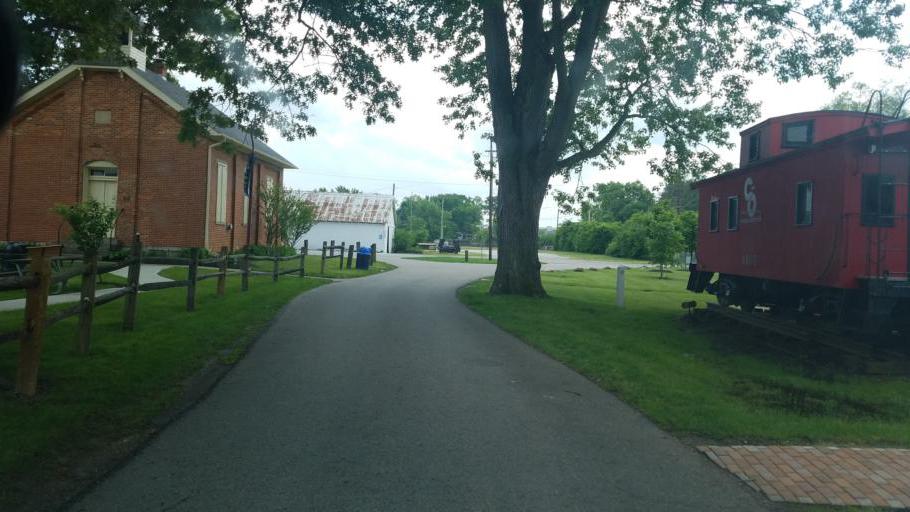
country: US
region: Ohio
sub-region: Franklin County
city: Hilliard
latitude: 40.0360
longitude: -83.1560
